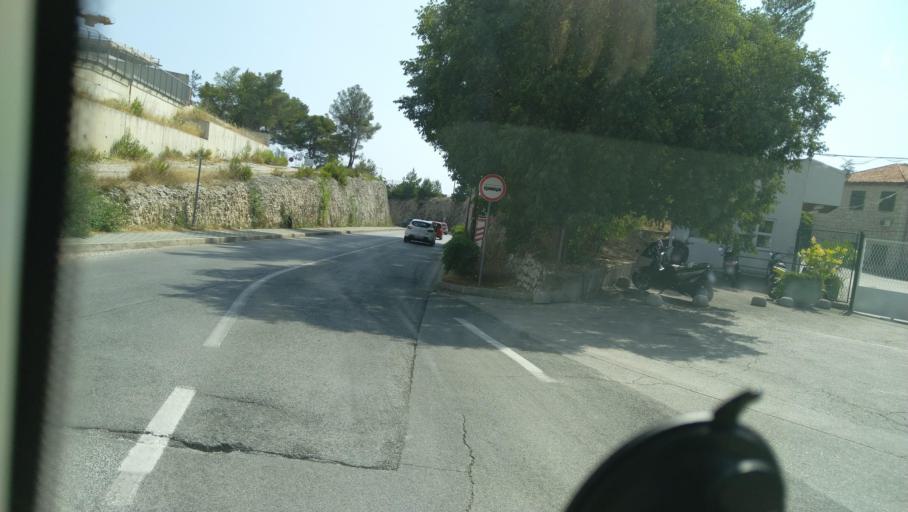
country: HR
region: Sibensko-Kniniska
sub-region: Grad Sibenik
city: Sibenik
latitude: 43.7220
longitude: 15.9072
